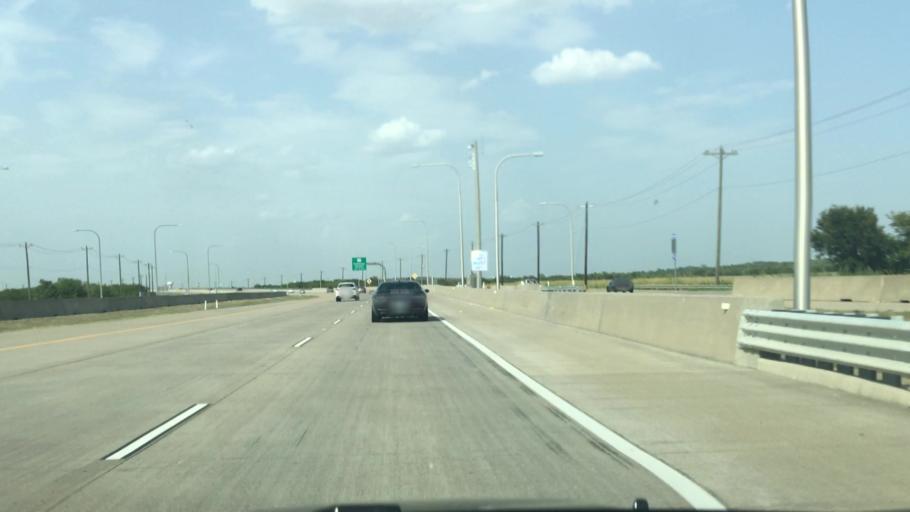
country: US
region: Texas
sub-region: Collin County
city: Prosper
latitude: 33.2018
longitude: -96.8253
